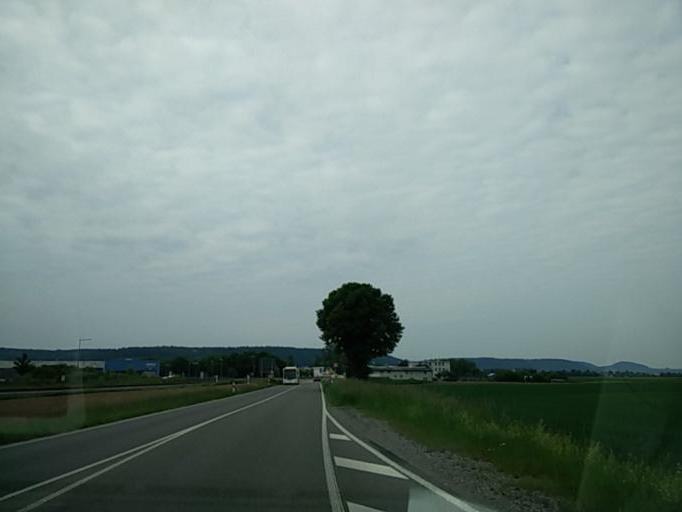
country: DE
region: Baden-Wuerttemberg
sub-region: Tuebingen Region
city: Tuebingen
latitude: 48.5001
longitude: 9.0324
